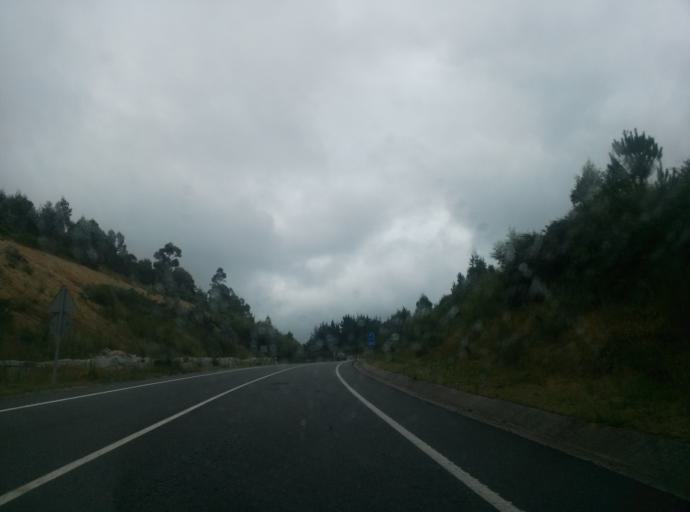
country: ES
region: Galicia
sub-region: Provincia de Lugo
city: Viveiro
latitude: 43.5971
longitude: -7.6106
